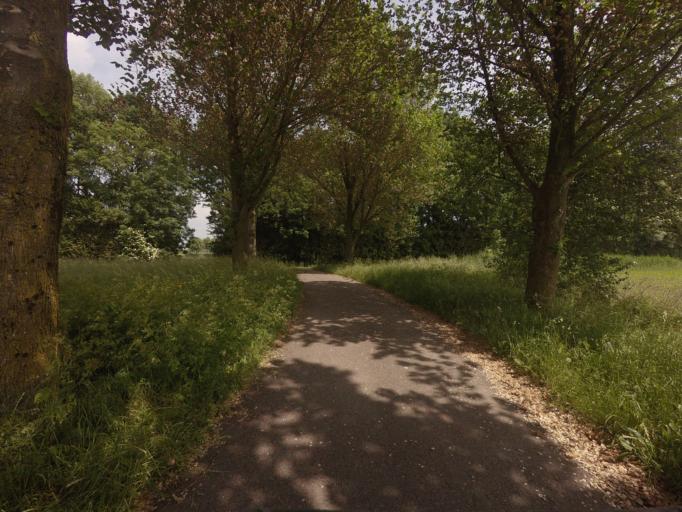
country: NL
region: Gelderland
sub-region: Gemeente Culemborg
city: Culemborg
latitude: 51.9987
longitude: 5.2087
